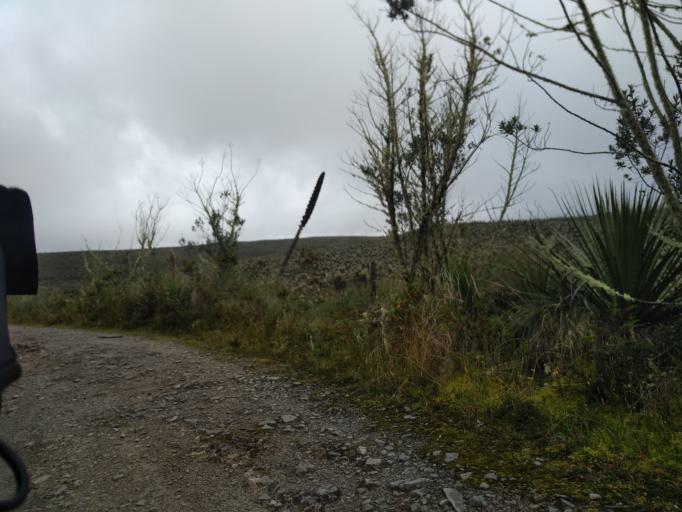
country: EC
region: Carchi
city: San Gabriel
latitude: 0.6903
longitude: -77.8504
